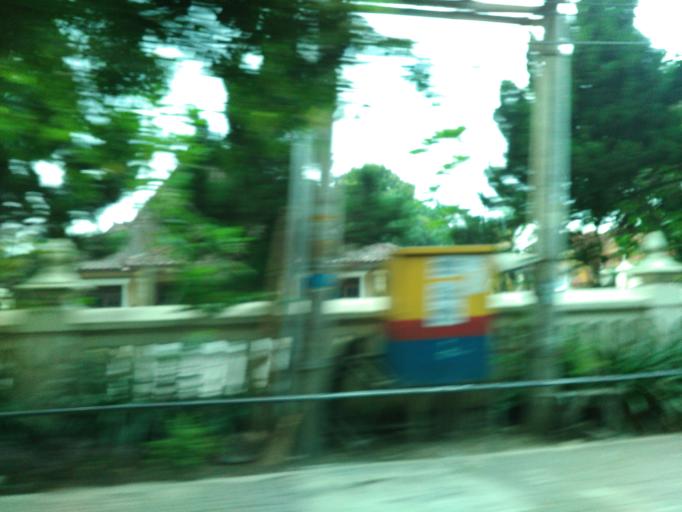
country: ID
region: Central Java
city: Delanggu
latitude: -7.6218
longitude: 110.7019
